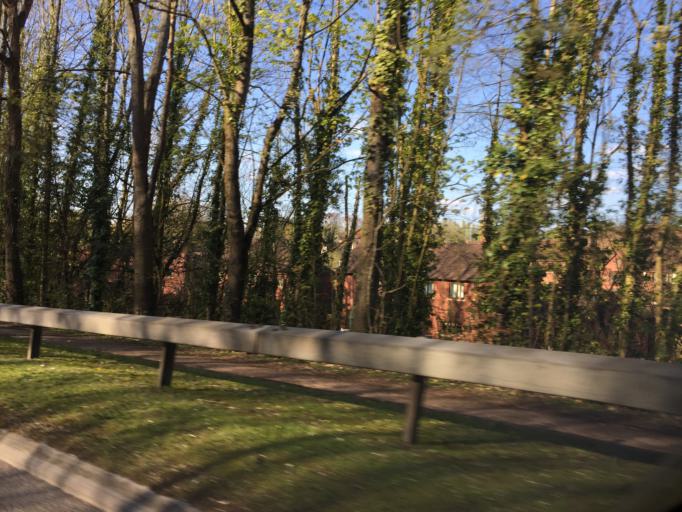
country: GB
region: Wales
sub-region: Torfaen County Borough
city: Cwmbran
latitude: 51.6234
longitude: -3.0123
